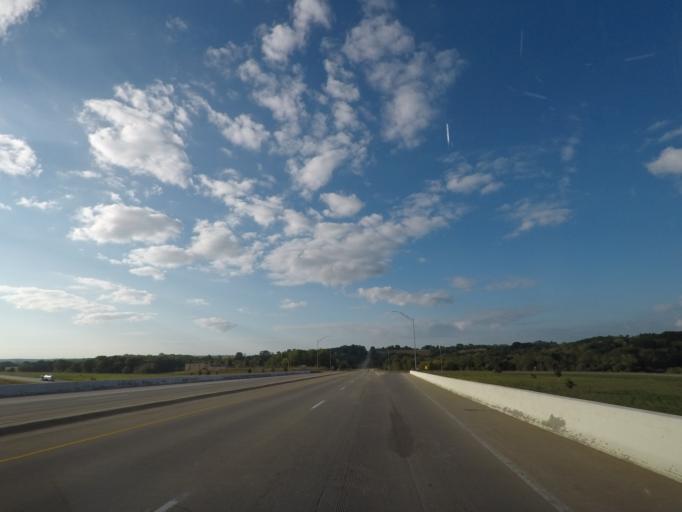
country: US
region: Iowa
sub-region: Warren County
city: Norwalk
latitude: 41.5082
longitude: -93.6451
